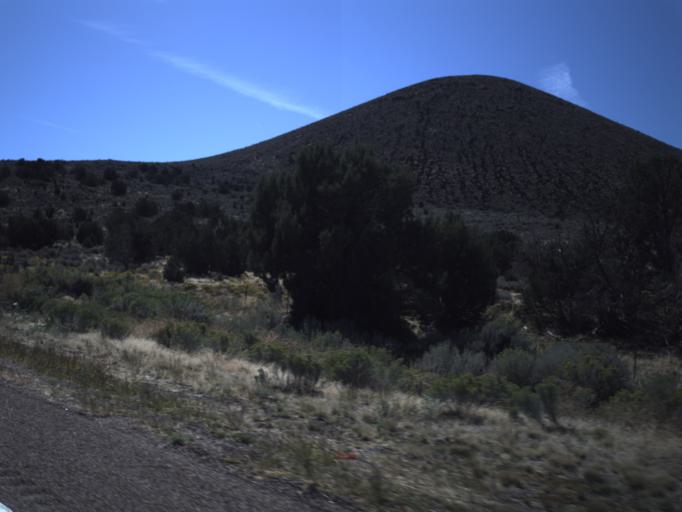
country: US
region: Utah
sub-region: Washington County
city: Ivins
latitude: 37.3235
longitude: -113.6925
